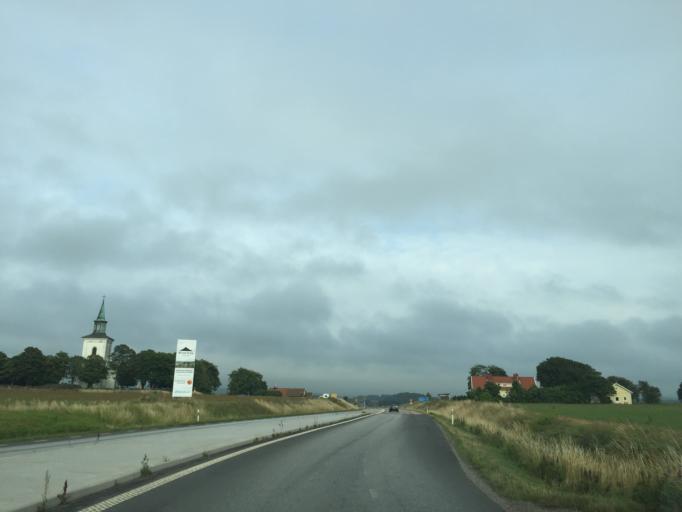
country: SE
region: Halland
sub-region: Falkenbergs Kommun
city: Falkenberg
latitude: 56.8843
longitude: 12.5702
